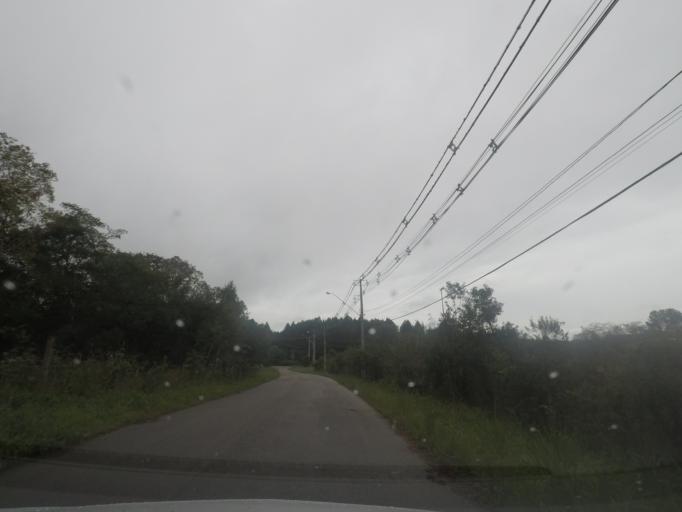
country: BR
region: Parana
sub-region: Campina Grande Do Sul
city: Campina Grande do Sul
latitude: -25.3147
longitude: -49.0752
